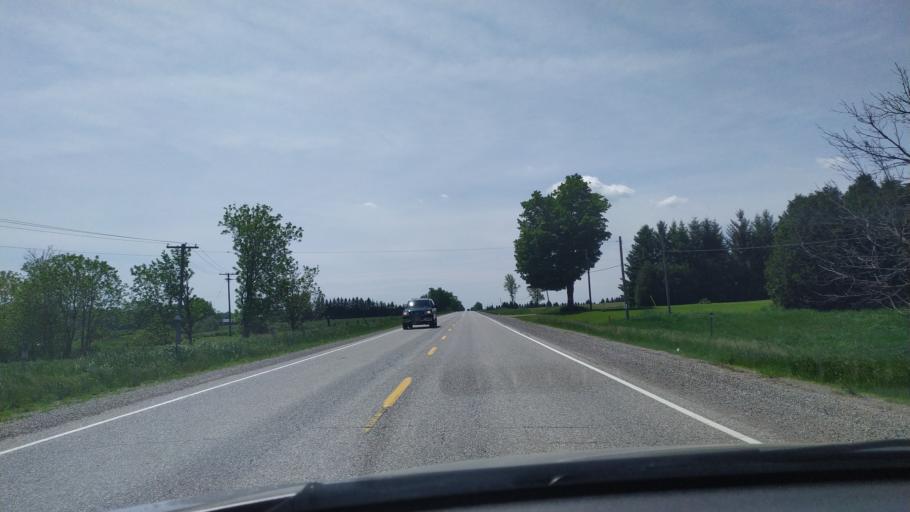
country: CA
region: Ontario
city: Dorchester
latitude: 43.1320
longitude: -81.0266
